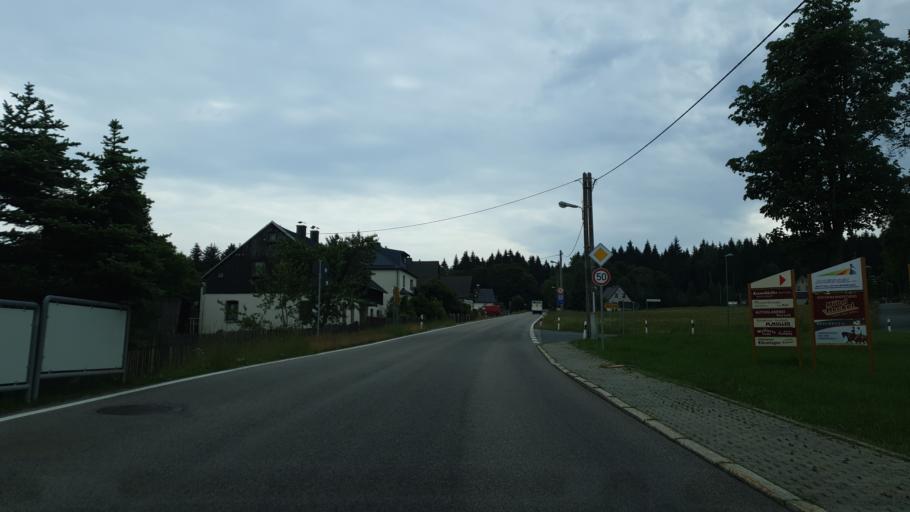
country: DE
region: Saxony
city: Auerbach
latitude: 50.4861
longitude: 12.4328
